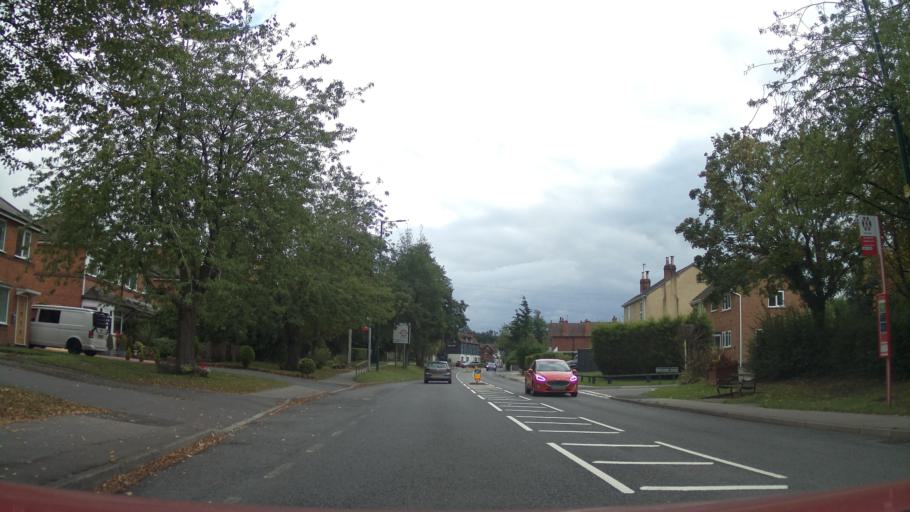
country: GB
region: England
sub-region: Solihull
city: Cheswick Green
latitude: 52.3554
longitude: -1.7783
